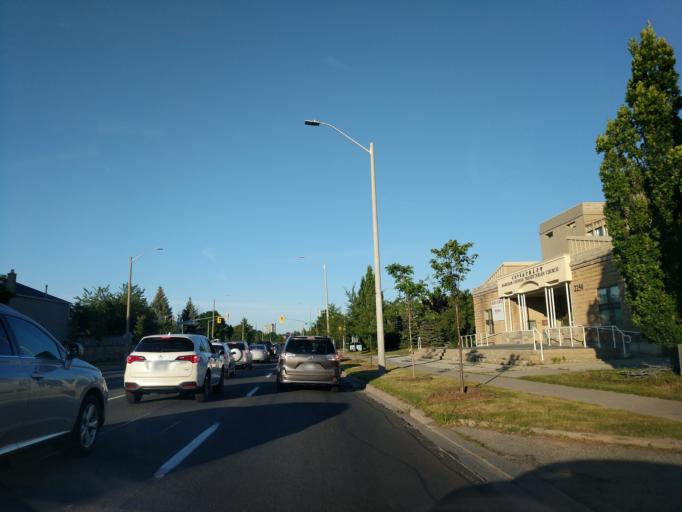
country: CA
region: Ontario
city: Markham
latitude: 43.8398
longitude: -79.2829
